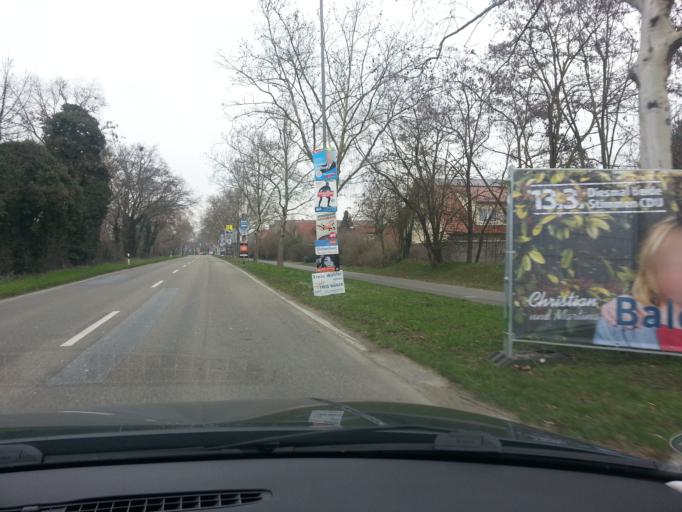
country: DE
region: Rheinland-Pfalz
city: Frankenthal
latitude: 49.5171
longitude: 8.3549
